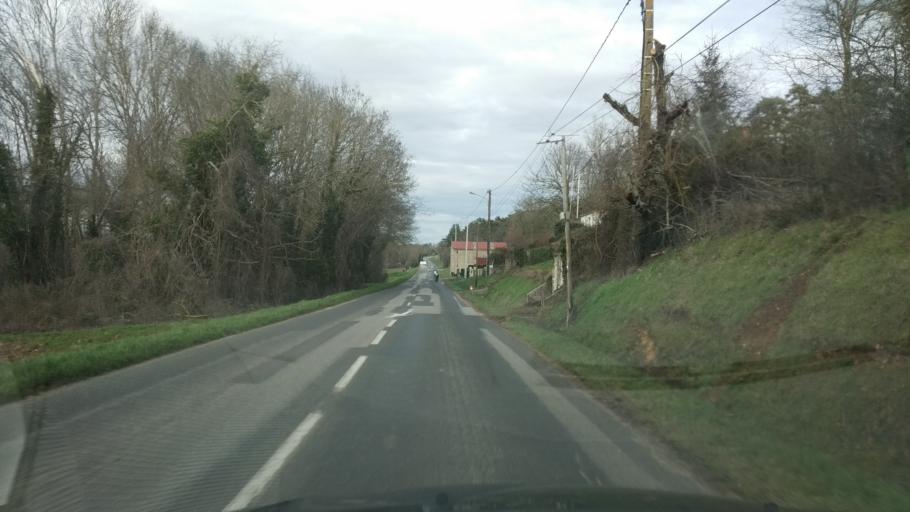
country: FR
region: Poitou-Charentes
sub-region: Departement de la Vienne
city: Chasseneuil-du-Poitou
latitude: 46.6516
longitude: 0.3881
